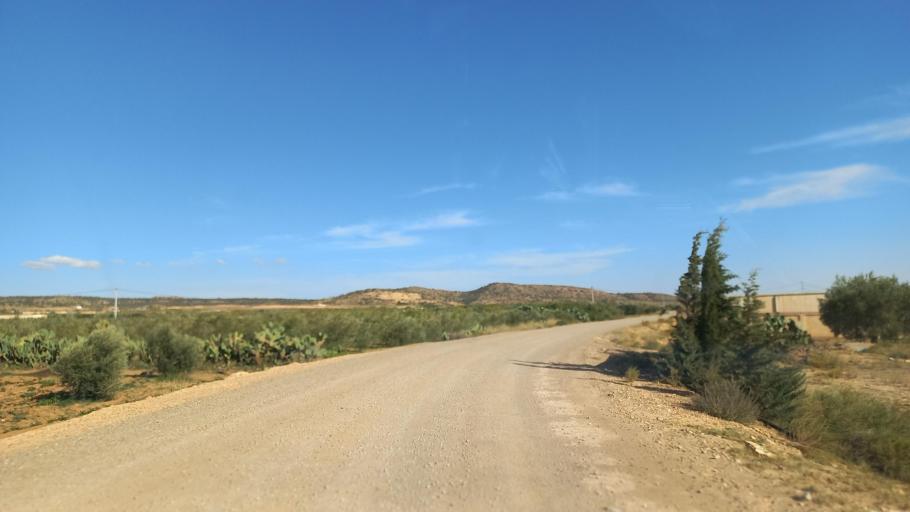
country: TN
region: Al Qasrayn
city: Sbiba
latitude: 35.2954
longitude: 9.1058
